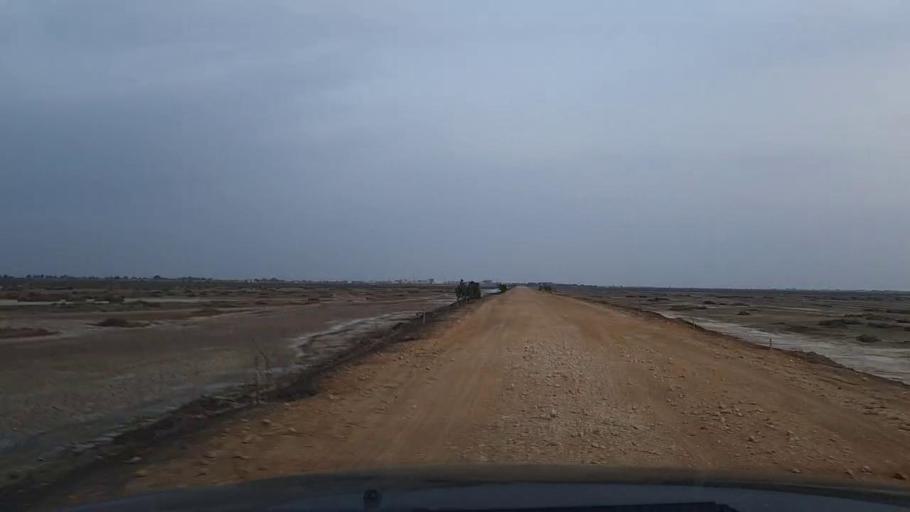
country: PK
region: Sindh
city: Jati
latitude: 24.4976
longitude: 68.3843
